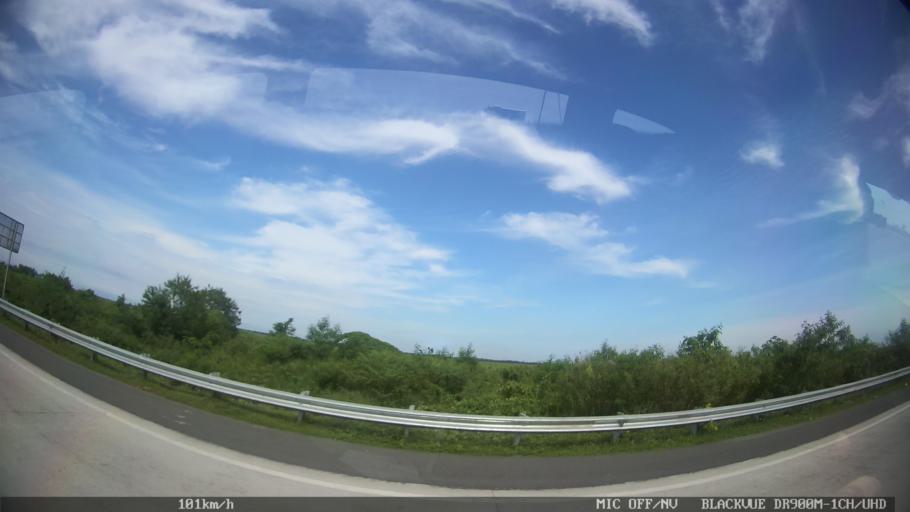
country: ID
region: North Sumatra
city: Binjai
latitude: 3.6719
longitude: 98.5347
